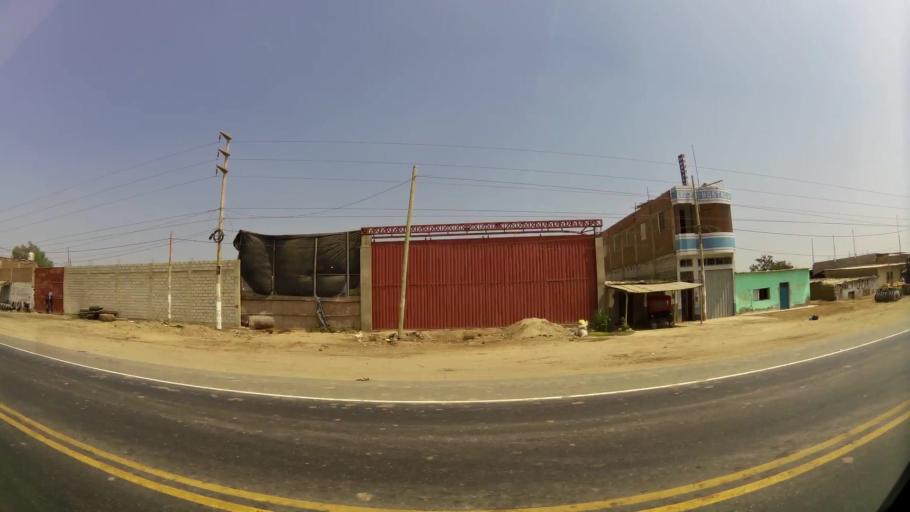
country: PE
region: La Libertad
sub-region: Chepen
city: Pacanga
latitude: -7.1525
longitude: -79.4482
